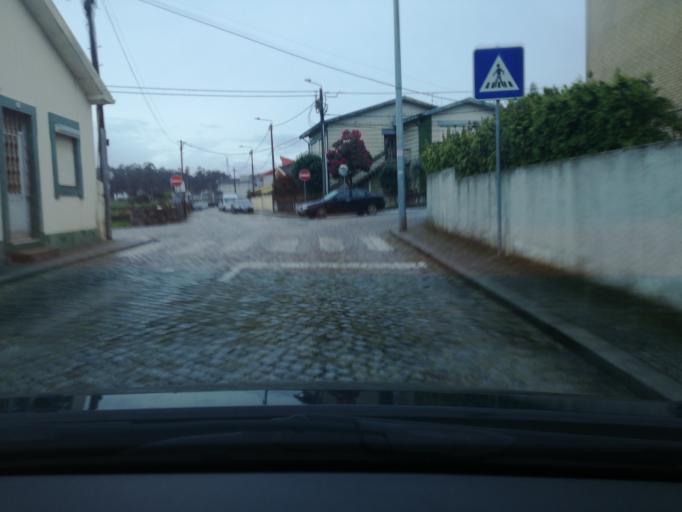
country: PT
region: Porto
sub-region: Maia
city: Anta
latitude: 41.2654
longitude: -8.6352
